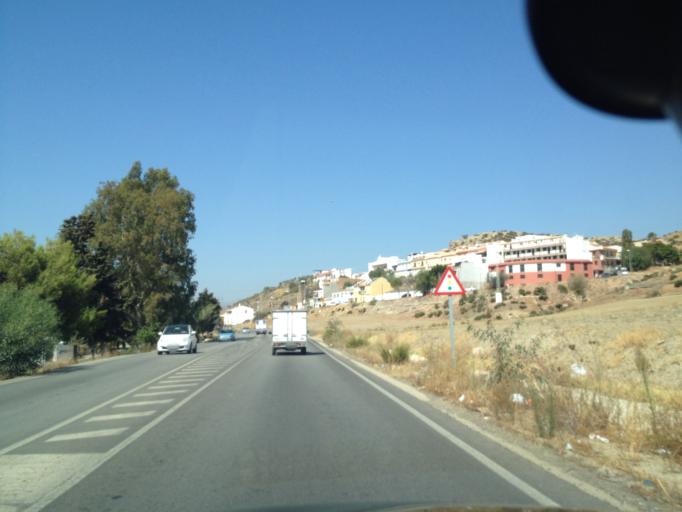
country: ES
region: Andalusia
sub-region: Provincia de Malaga
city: Estacion de Cartama
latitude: 36.7332
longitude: -4.5718
